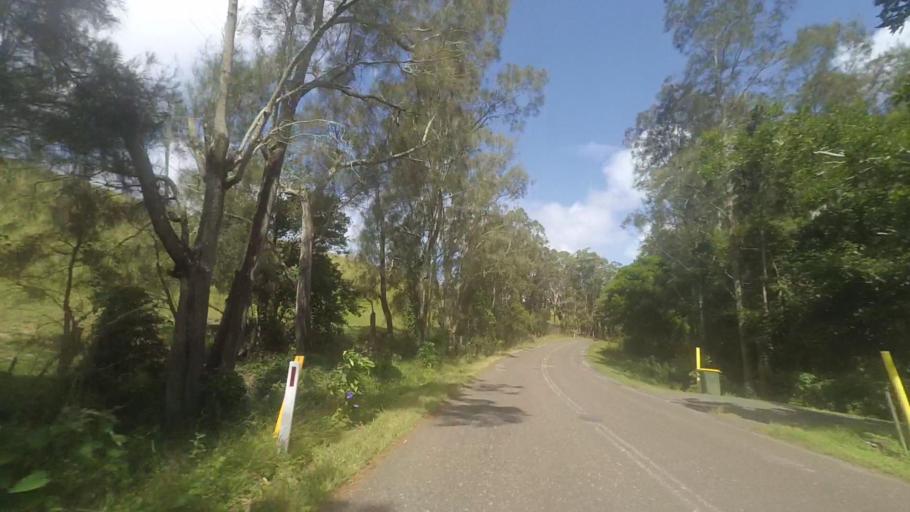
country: AU
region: New South Wales
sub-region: Great Lakes
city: Bulahdelah
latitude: -32.3918
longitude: 152.4358
